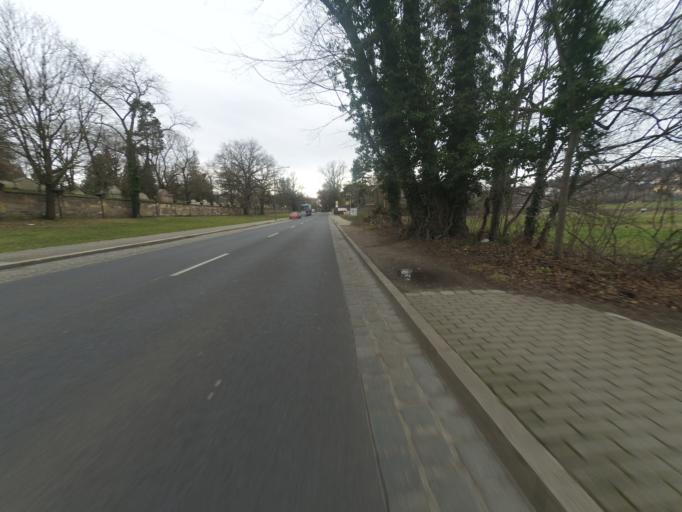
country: DE
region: Saxony
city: Albertstadt
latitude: 51.0387
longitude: 13.8193
